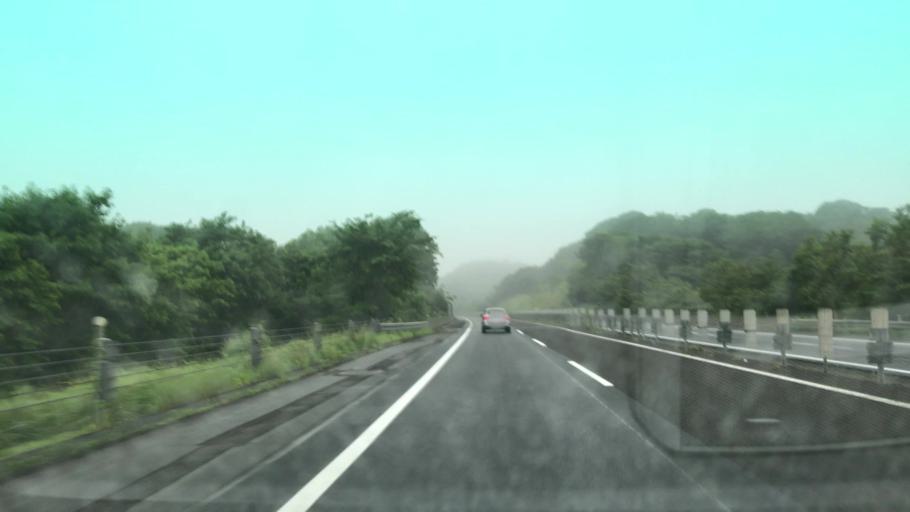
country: JP
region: Hokkaido
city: Tomakomai
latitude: 42.6388
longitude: 141.5060
